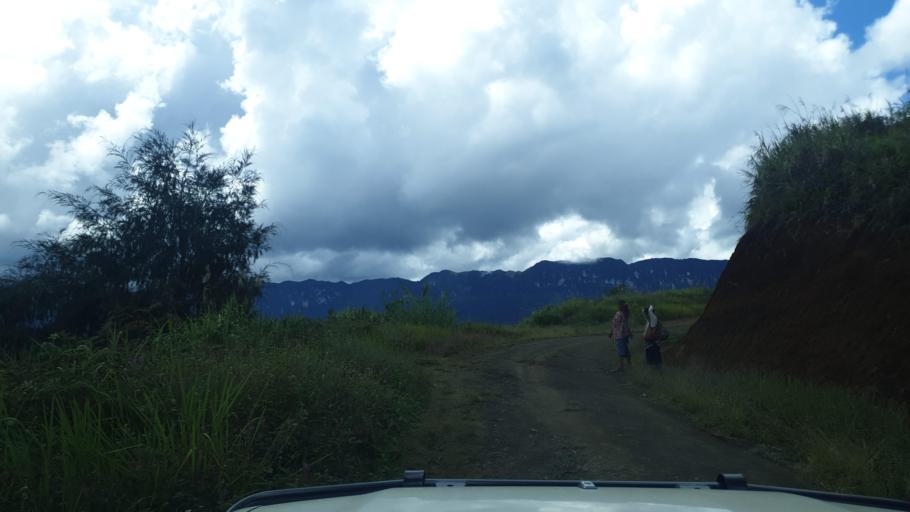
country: PG
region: Eastern Highlands
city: Goroka
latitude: -6.2765
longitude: 145.1898
